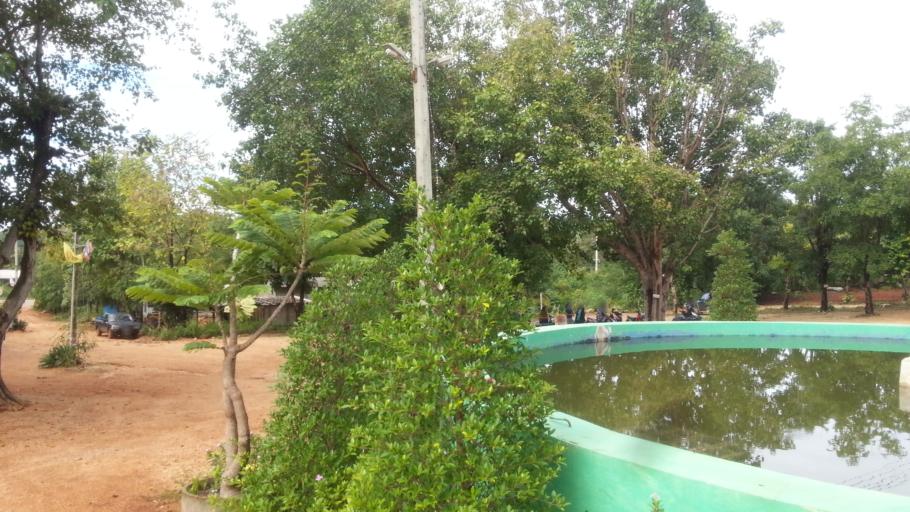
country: TH
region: Kanchanaburi
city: Sai Yok
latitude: 14.1157
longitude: 99.1917
